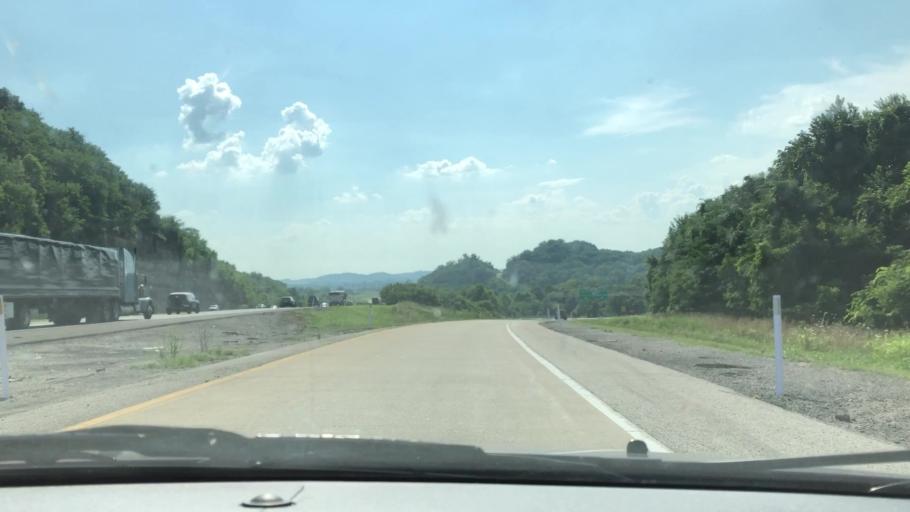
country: US
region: Tennessee
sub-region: Williamson County
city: Thompson's Station
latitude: 35.8227
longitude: -86.8279
